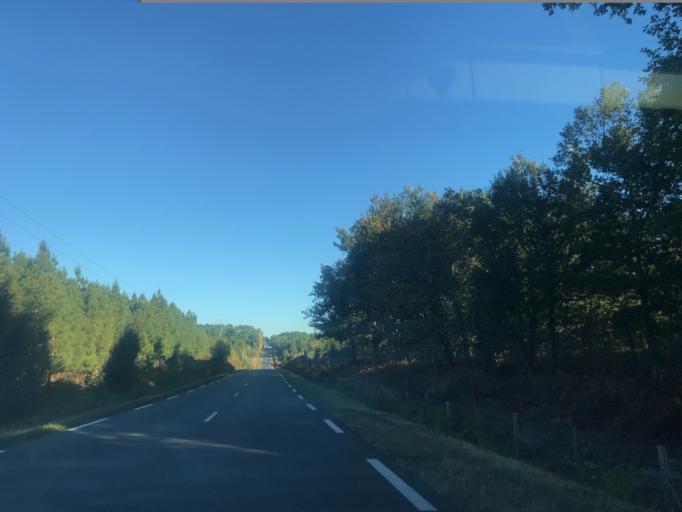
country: FR
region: Poitou-Charentes
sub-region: Departement de la Charente-Maritime
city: Saint-Aigulin
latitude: 45.1719
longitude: -0.0631
